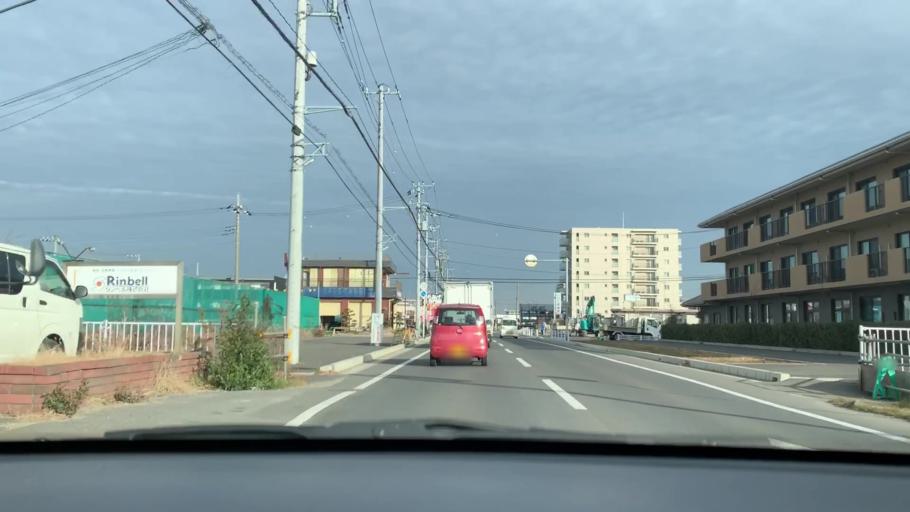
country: JP
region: Chiba
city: Nagareyama
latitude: 35.8281
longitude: 139.8957
